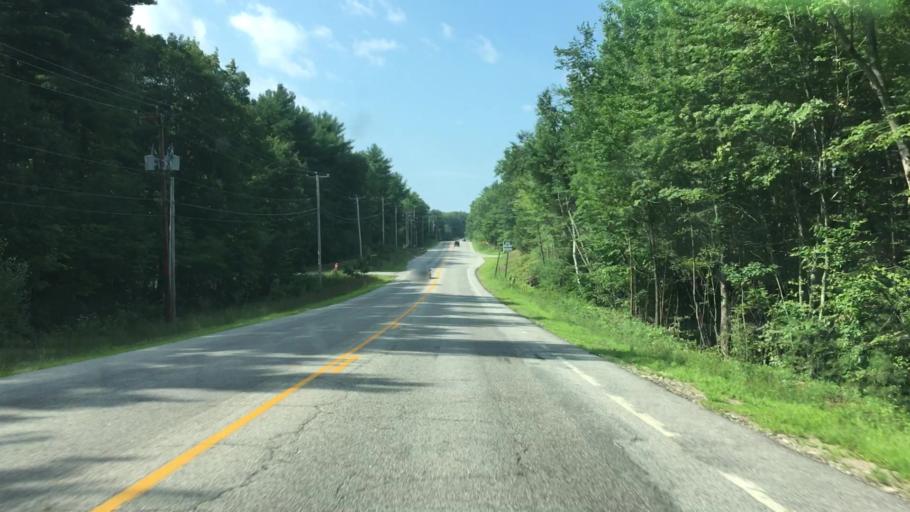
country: US
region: Maine
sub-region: Androscoggin County
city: Poland
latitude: 44.0257
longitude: -70.3491
